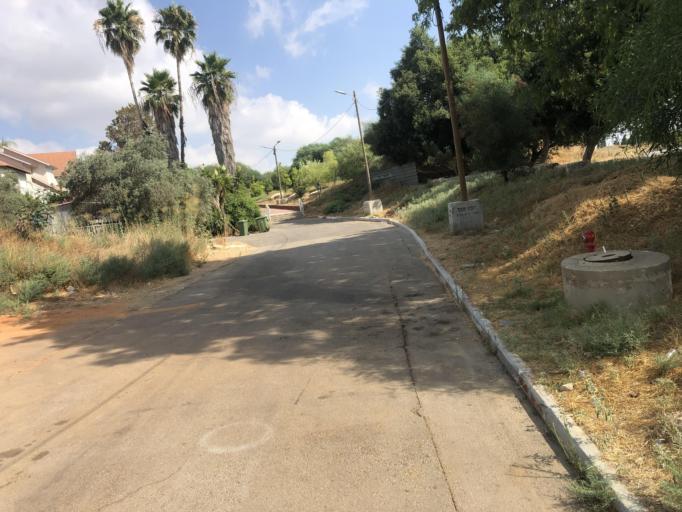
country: IL
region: Central District
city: Yehud
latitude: 32.0388
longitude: 34.8911
